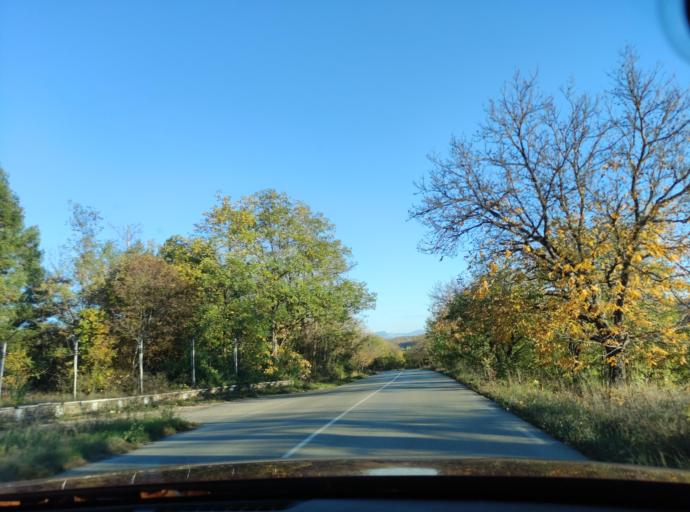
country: BG
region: Montana
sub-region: Obshtina Montana
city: Montana
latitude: 43.3968
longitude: 23.1133
